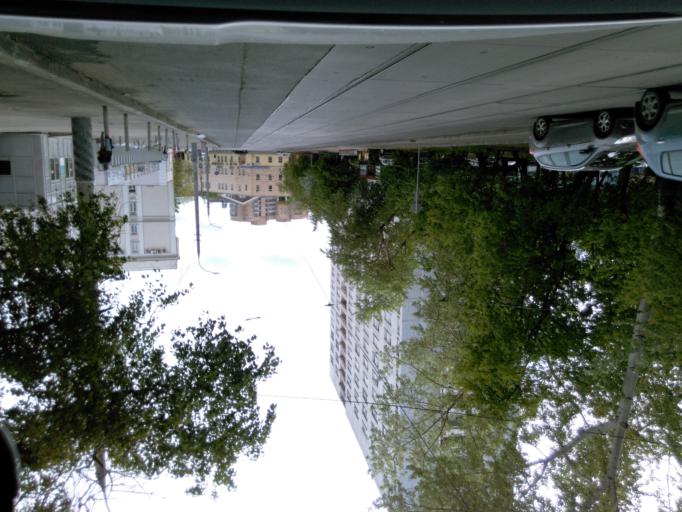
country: RU
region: Moscow
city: Mar'ina Roshcha
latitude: 55.7897
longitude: 37.6099
